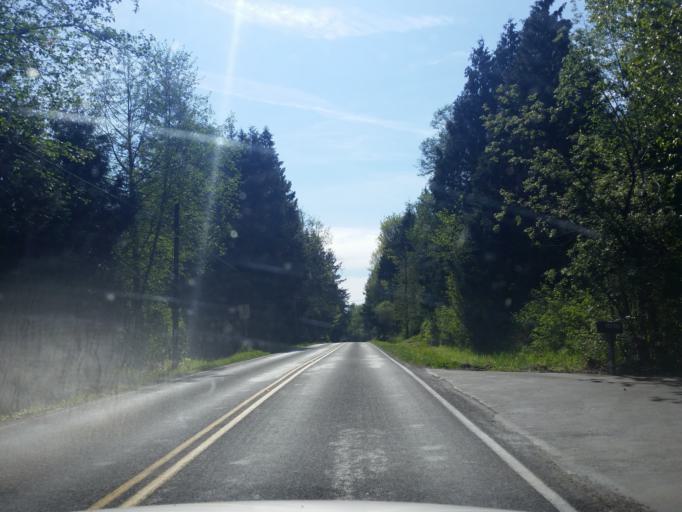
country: US
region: Washington
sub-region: Snohomish County
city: Machias
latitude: 47.9585
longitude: -122.0556
